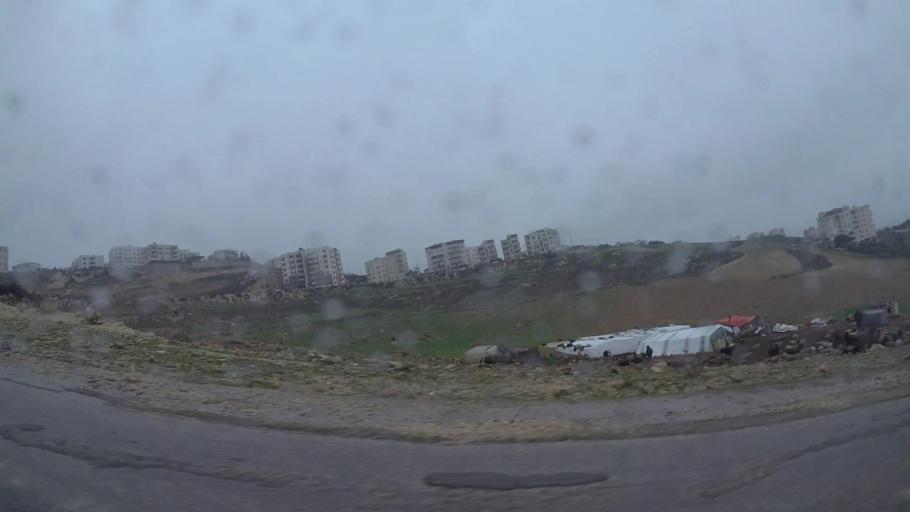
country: JO
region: Amman
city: Al Jubayhah
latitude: 32.0351
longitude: 35.8487
